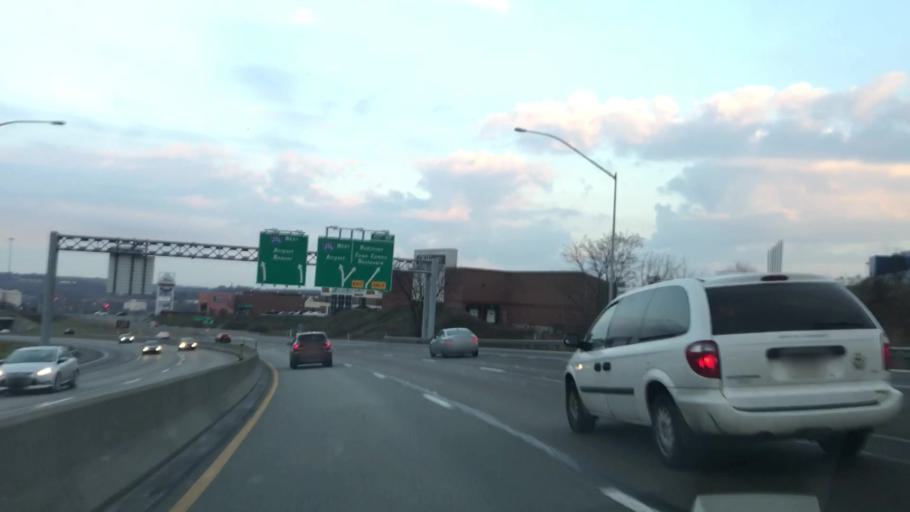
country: US
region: Pennsylvania
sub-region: Allegheny County
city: Oakdale
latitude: 40.4524
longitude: -80.1691
